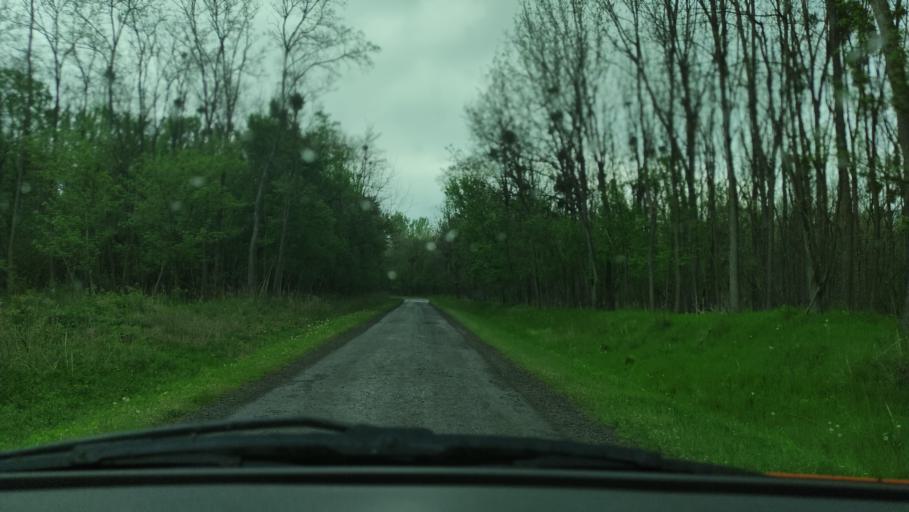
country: HU
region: Baranya
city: Mohacs
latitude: 45.9106
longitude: 18.7529
